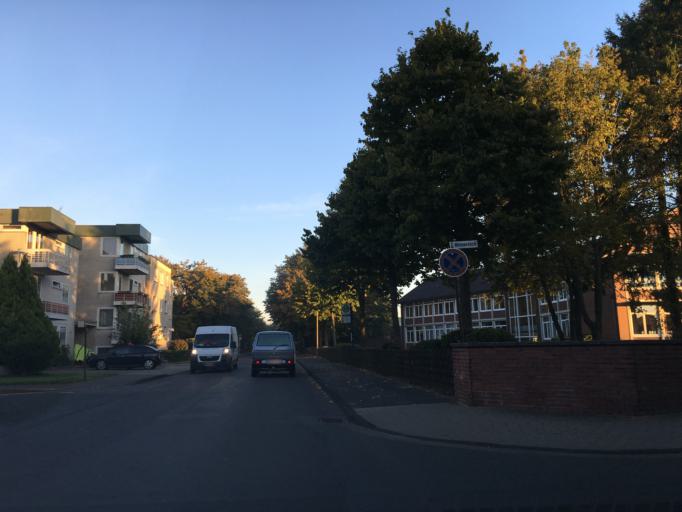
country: DE
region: North Rhine-Westphalia
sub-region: Regierungsbezirk Munster
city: Steinfurt
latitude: 52.1416
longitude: 7.3265
